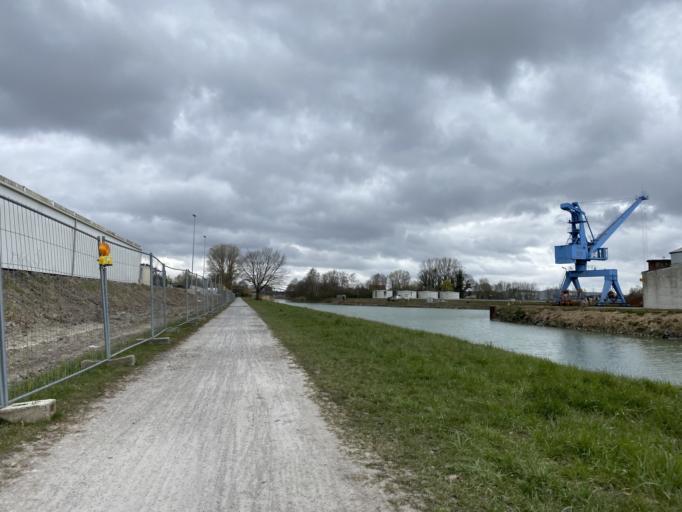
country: DE
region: North Rhine-Westphalia
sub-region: Regierungsbezirk Arnsberg
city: Welver
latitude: 51.6850
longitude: 7.9419
